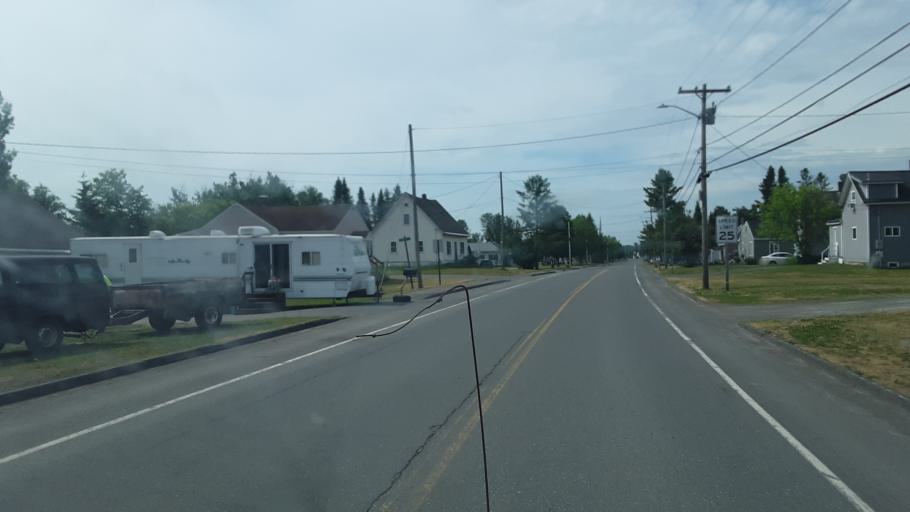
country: US
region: Maine
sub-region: Aroostook County
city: Caribou
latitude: 46.7992
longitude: -68.1556
